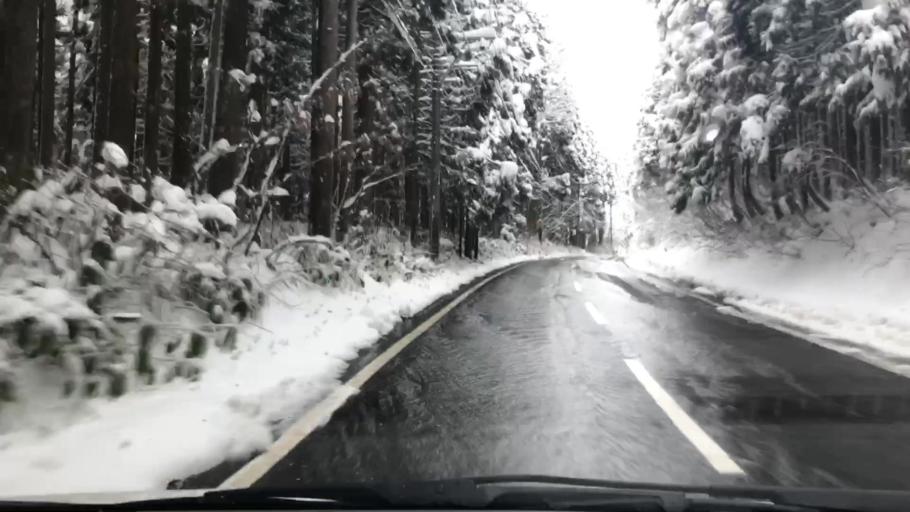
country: JP
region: Toyama
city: Kamiichi
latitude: 36.5763
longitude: 137.4070
